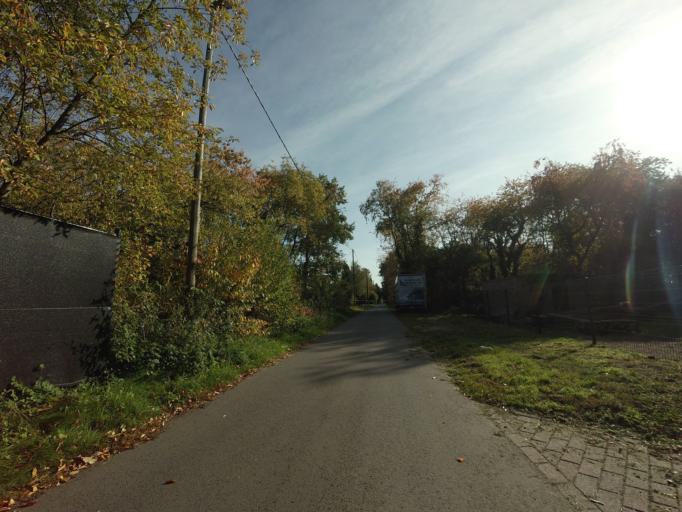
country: BE
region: Flanders
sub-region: Provincie Antwerpen
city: Stabroek
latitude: 51.3523
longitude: 4.3320
